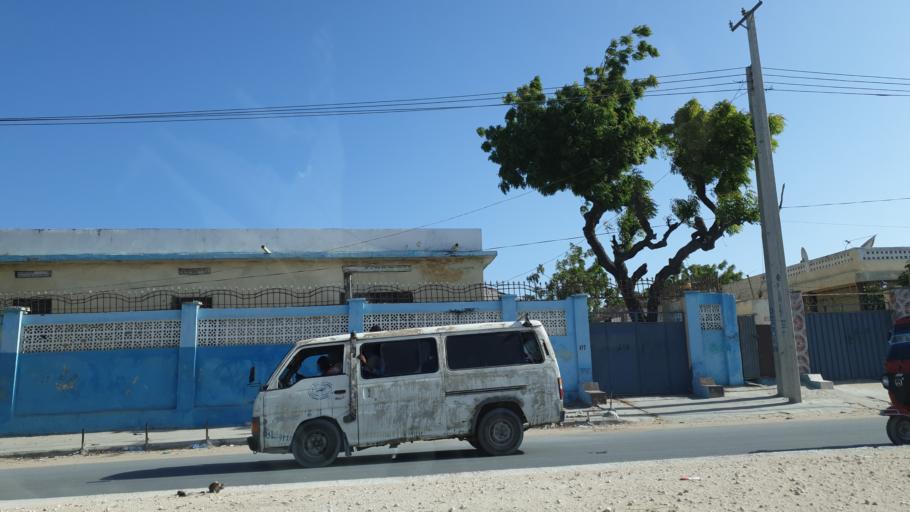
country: SO
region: Banaadir
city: Mogadishu
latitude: 2.0518
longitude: 45.3110
